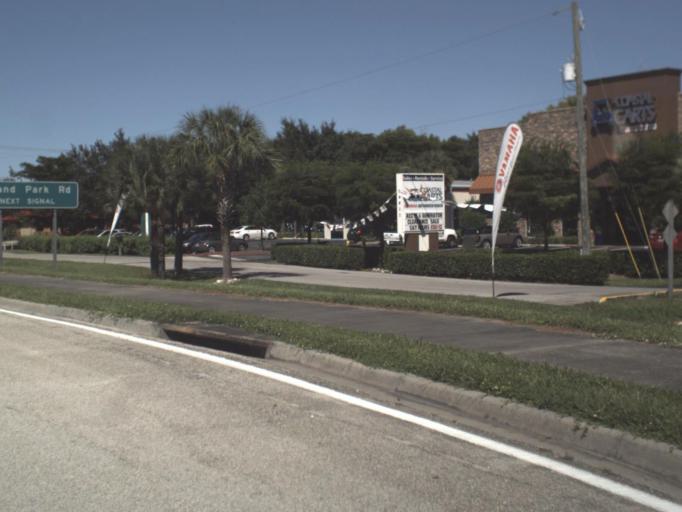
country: US
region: Florida
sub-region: Lee County
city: Villas
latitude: 26.5006
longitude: -81.8548
